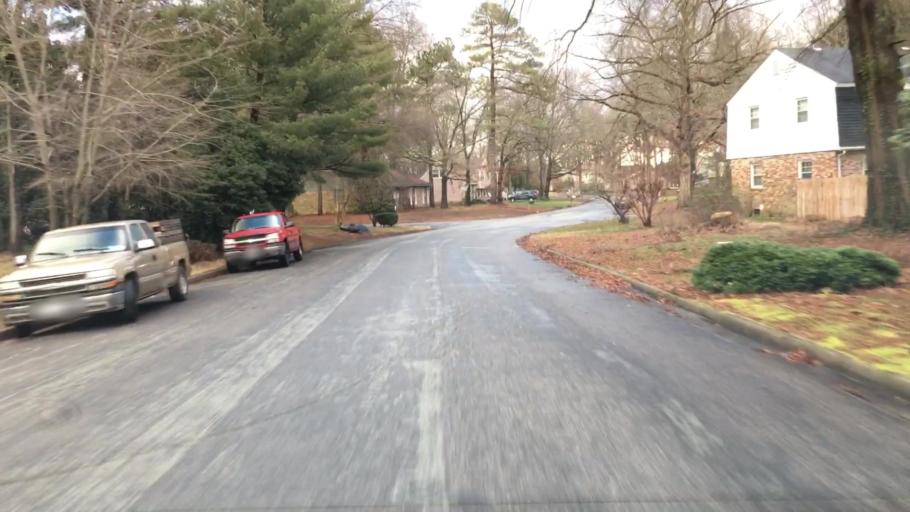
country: US
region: Virginia
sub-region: Chesterfield County
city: Bon Air
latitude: 37.5126
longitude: -77.6204
